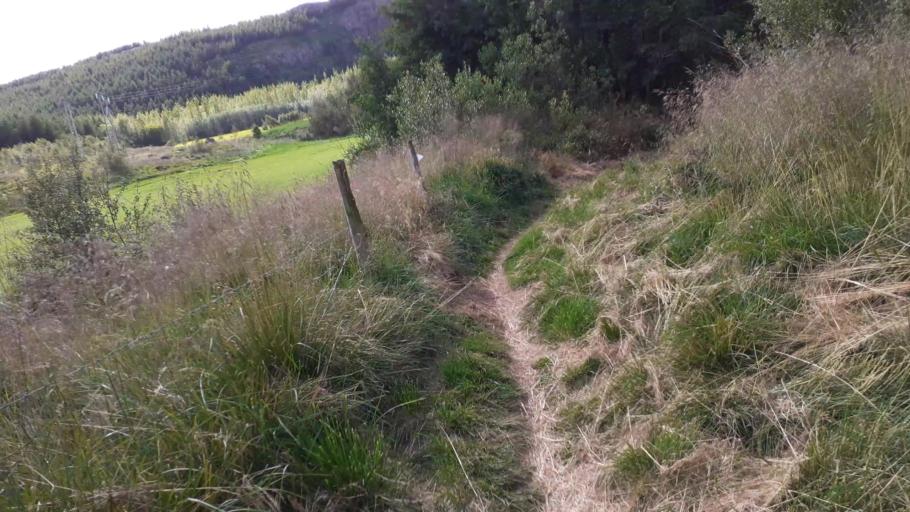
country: IS
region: Northeast
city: Akureyri
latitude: 65.6402
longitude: -18.0859
